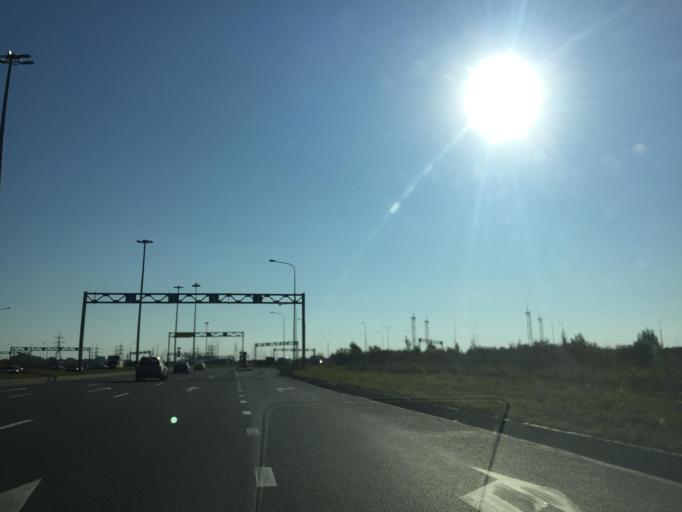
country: RU
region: St.-Petersburg
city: Metallostroy
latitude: 59.7501
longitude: 30.5285
